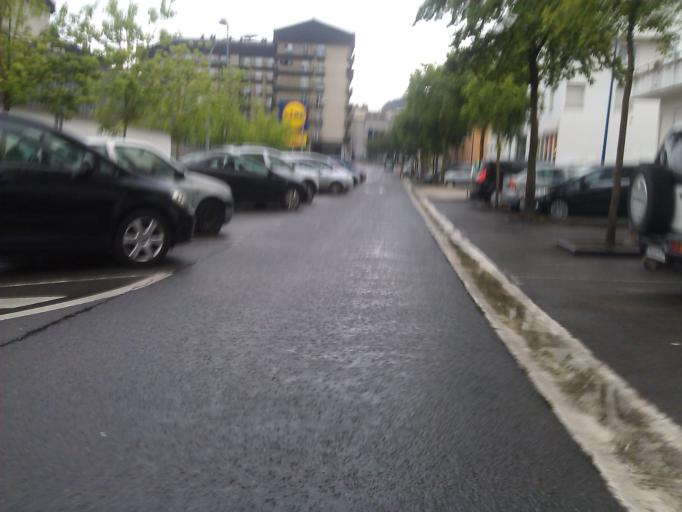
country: ES
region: Basque Country
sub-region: Provincia de Guipuzcoa
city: Hernani
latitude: 43.2712
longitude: -1.9717
